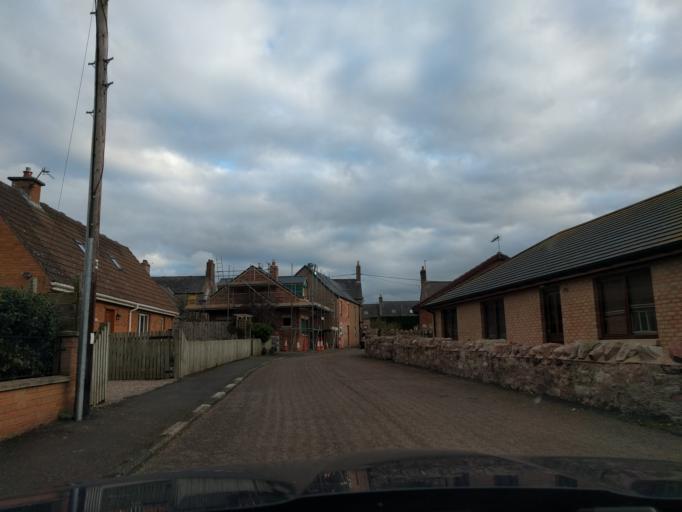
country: GB
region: Scotland
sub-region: The Scottish Borders
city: Allanton
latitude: 55.7424
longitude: -2.1147
